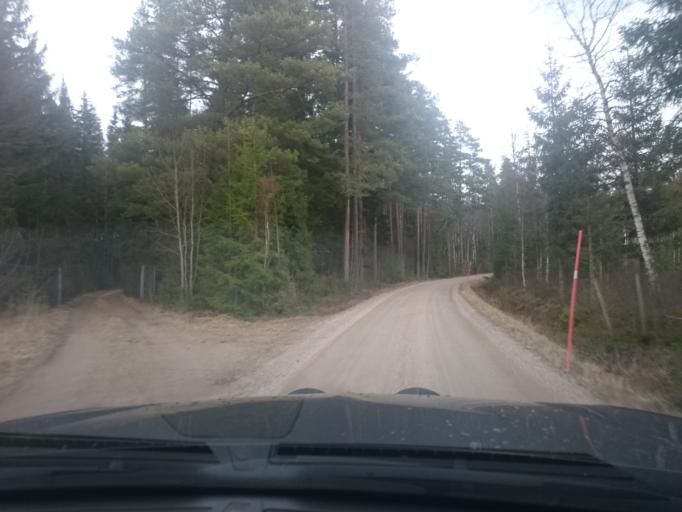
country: SE
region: Joenkoeping
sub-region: Vetlanda Kommun
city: Vetlanda
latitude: 57.2931
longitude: 15.1522
